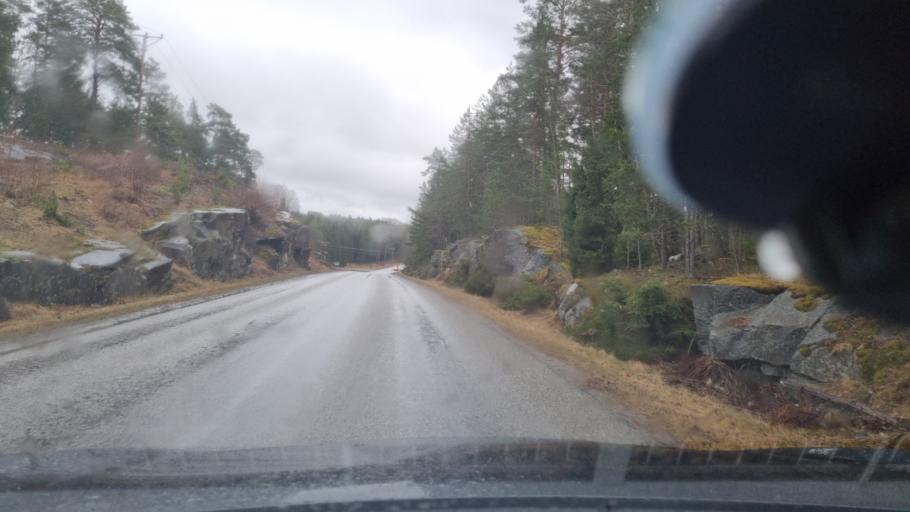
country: SE
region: Stockholm
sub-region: Sigtuna Kommun
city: Sigtuna
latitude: 59.5596
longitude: 17.7145
